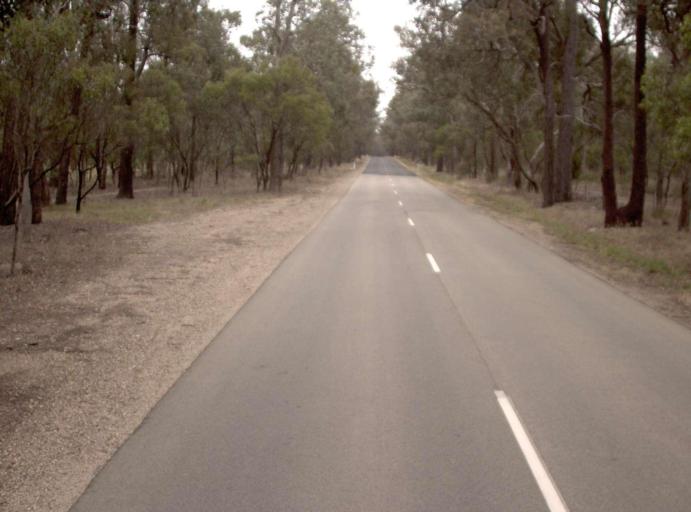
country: AU
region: Victoria
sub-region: Wellington
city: Heyfield
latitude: -37.9576
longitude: 146.7720
